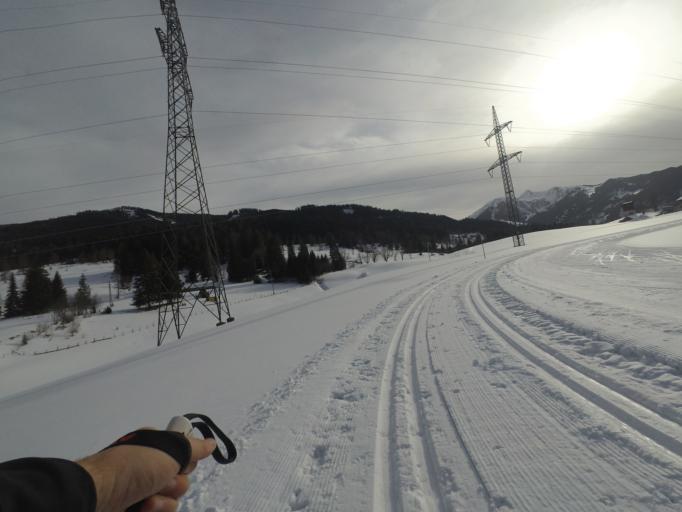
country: AT
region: Salzburg
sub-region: Politischer Bezirk Zell am See
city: Taxenbach
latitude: 47.2884
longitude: 12.9941
